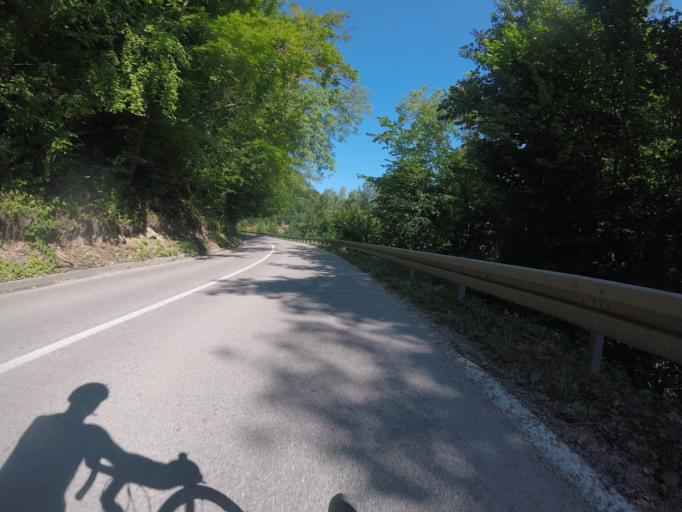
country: HR
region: Zagrebacka
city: Bregana
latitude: 45.8410
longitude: 15.6685
